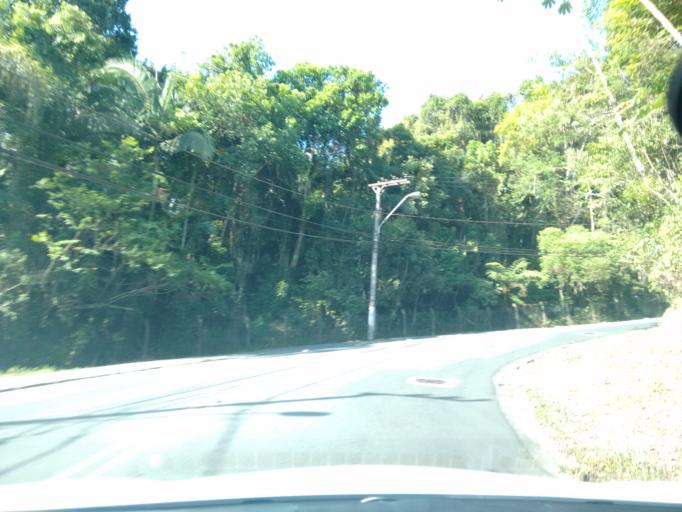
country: BR
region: Santa Catarina
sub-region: Blumenau
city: Blumenau
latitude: -26.9066
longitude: -49.0723
